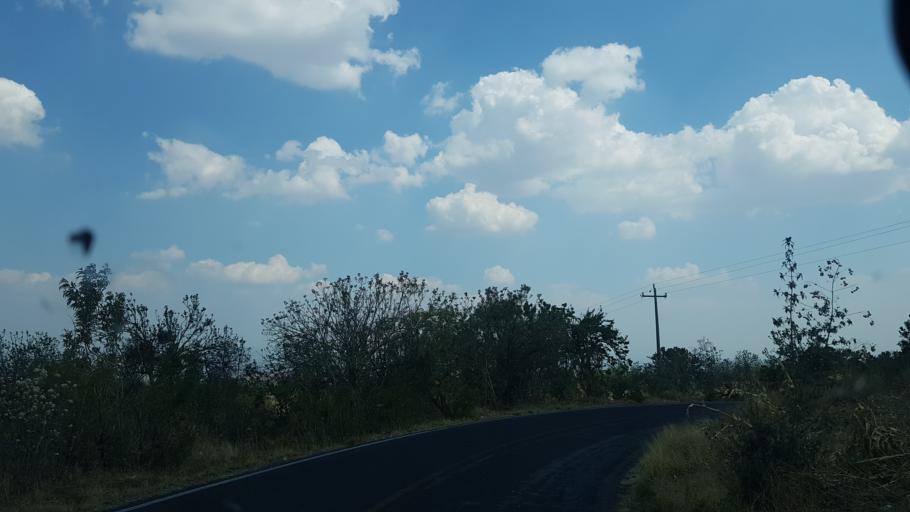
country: MX
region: Puebla
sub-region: Atlixco
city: San Pedro Benito Juarez
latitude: 18.9447
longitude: -98.5354
